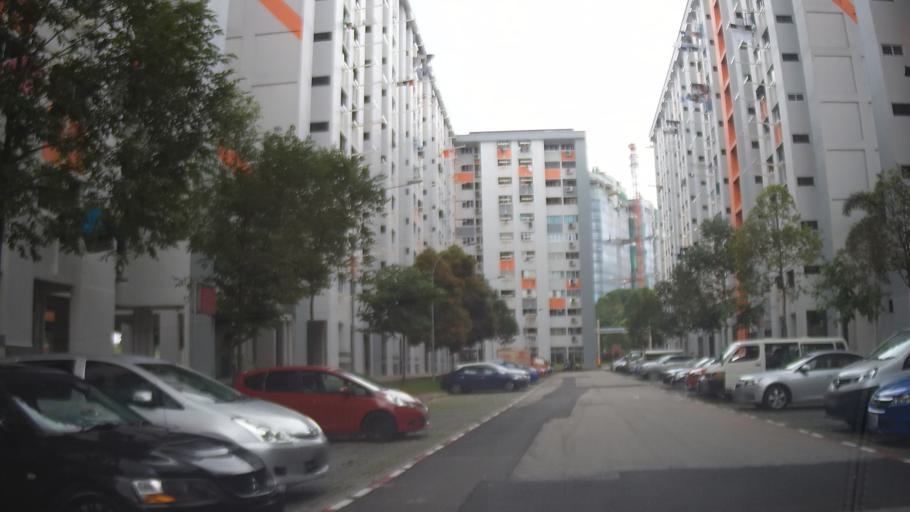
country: MY
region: Johor
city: Johor Bahru
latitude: 1.4331
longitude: 103.7818
